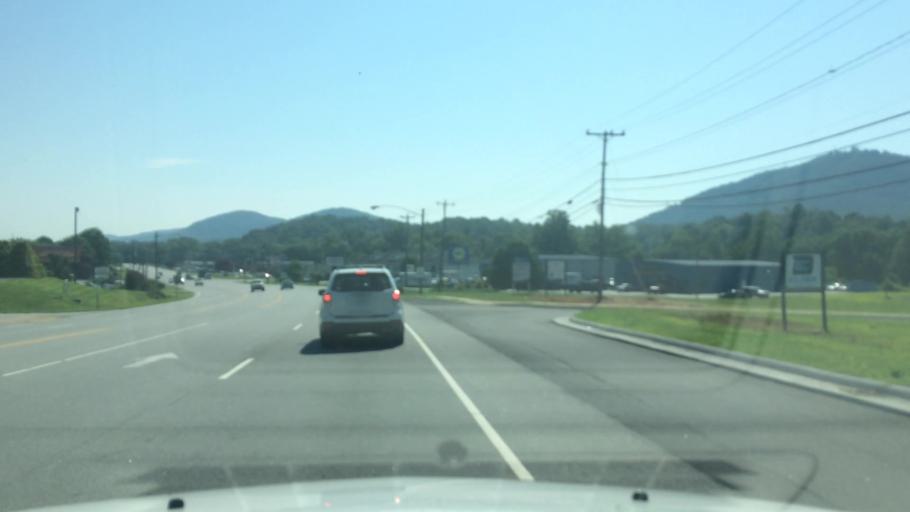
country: US
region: North Carolina
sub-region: Caldwell County
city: Lenoir
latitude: 35.9153
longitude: -81.5200
